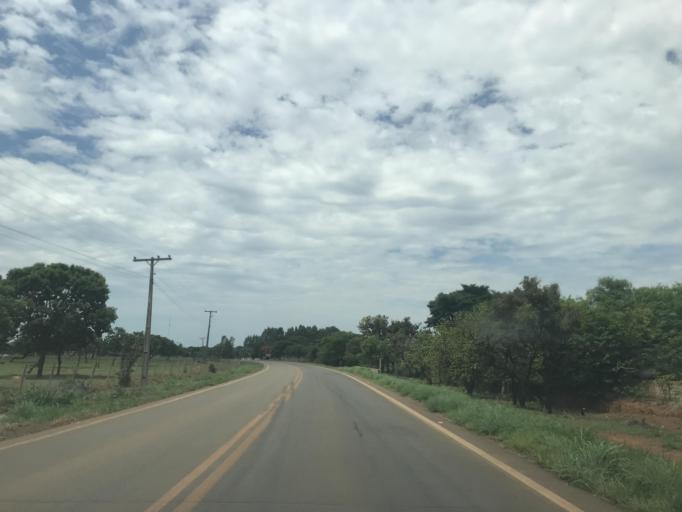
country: BR
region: Goias
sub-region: Luziania
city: Luziania
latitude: -16.3237
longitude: -48.0191
